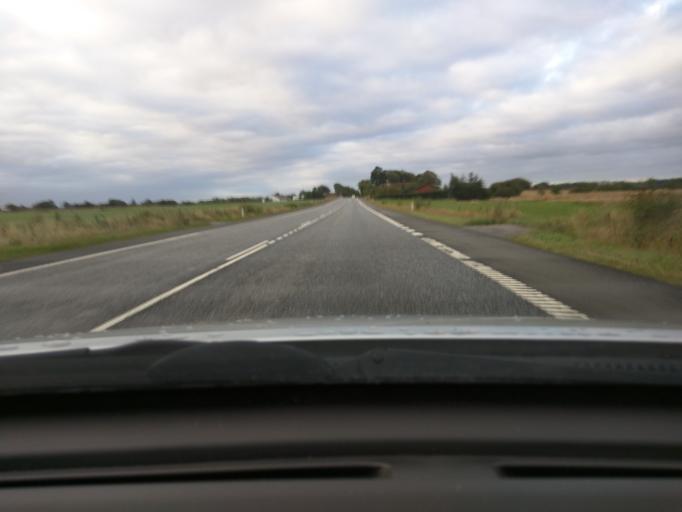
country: DK
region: Central Jutland
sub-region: Silkeborg Kommune
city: Kjellerup
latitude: 56.2843
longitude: 9.3202
